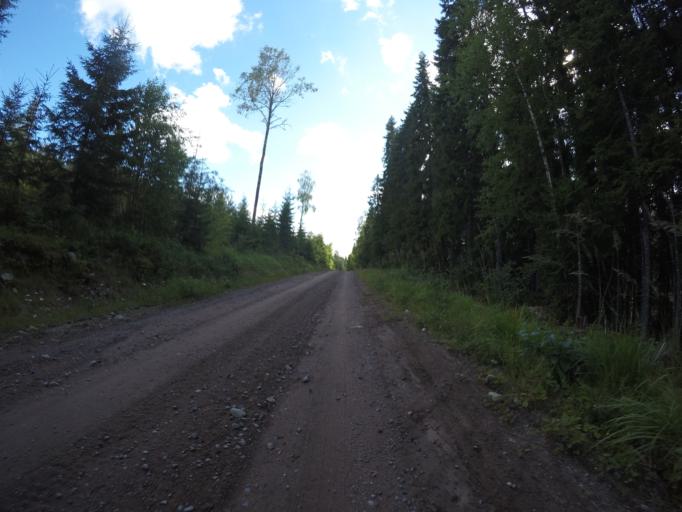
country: SE
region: OErebro
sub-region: Hallefors Kommun
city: Haellefors
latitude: 60.0046
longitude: 14.6087
